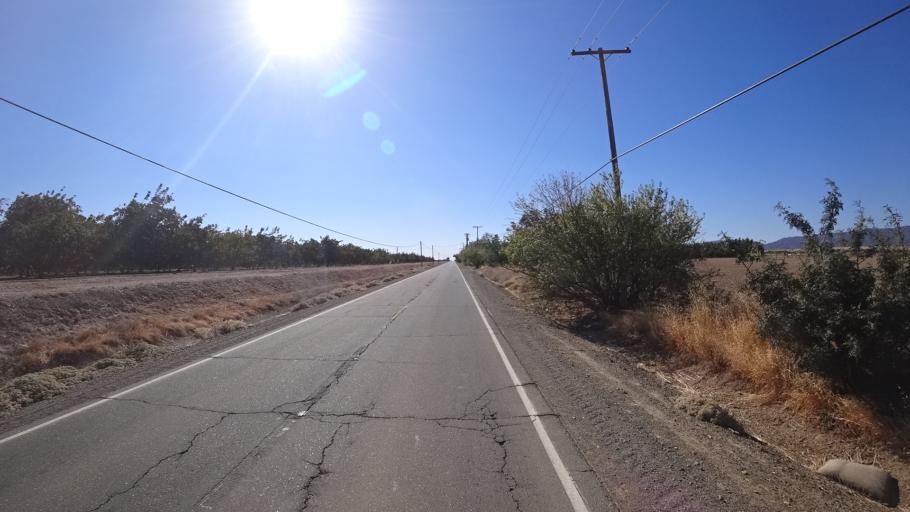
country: US
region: California
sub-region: Yolo County
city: Cottonwood
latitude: 38.5967
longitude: -121.9714
